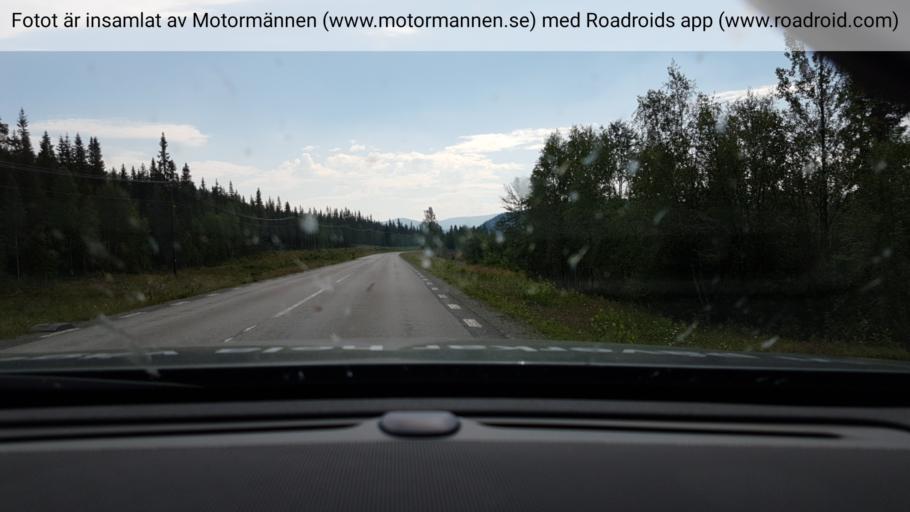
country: SE
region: Vaesterbotten
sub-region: Vilhelmina Kommun
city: Sjoberg
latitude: 65.5185
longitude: 15.6402
